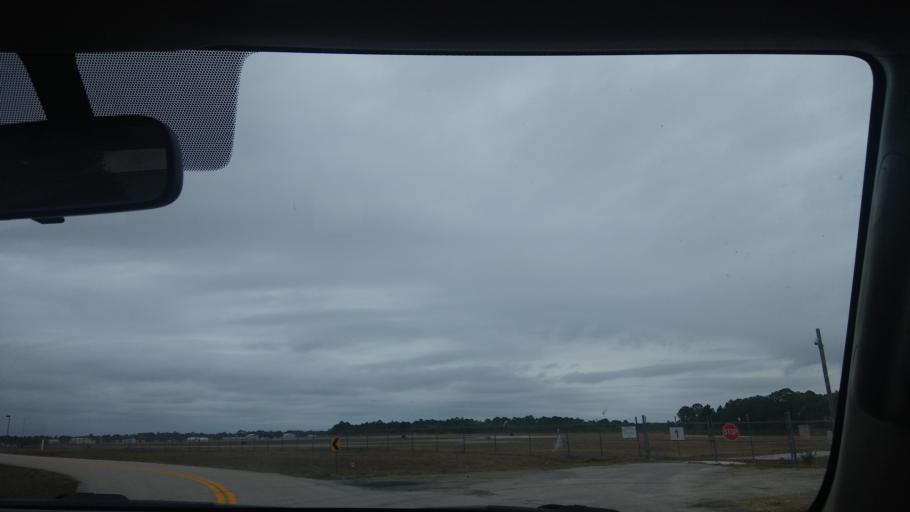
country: US
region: Florida
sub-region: Indian River County
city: Sebastian
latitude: 27.8130
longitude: -80.4893
